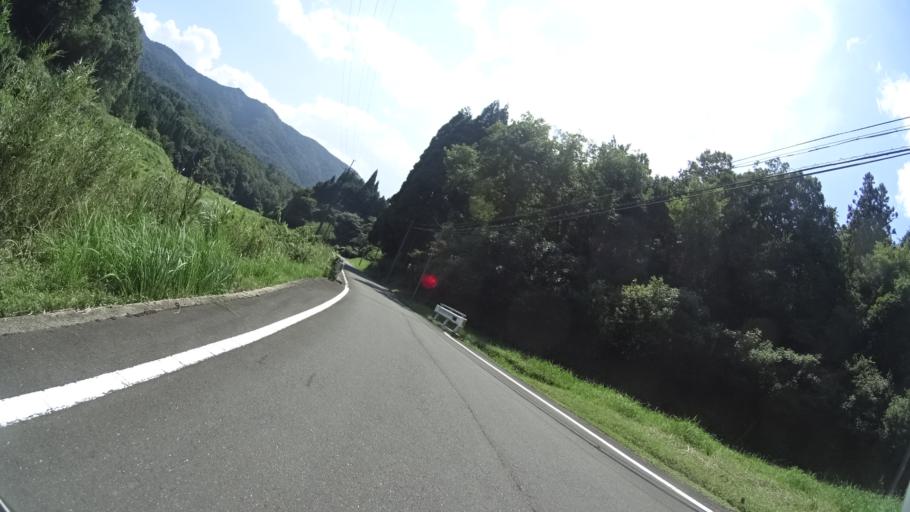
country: JP
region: Kyoto
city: Maizuru
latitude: 35.3816
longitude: 135.3532
